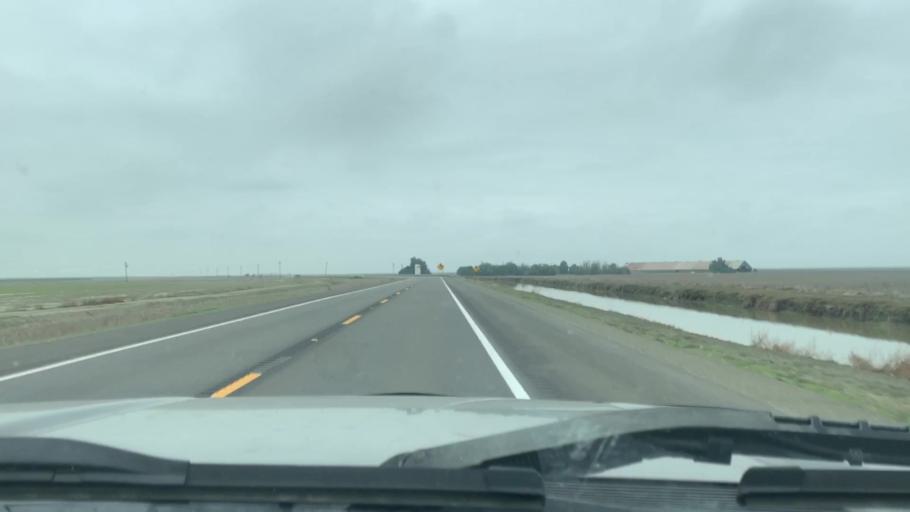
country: US
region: California
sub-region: Kings County
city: Kettleman City
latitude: 36.0465
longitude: -119.9484
